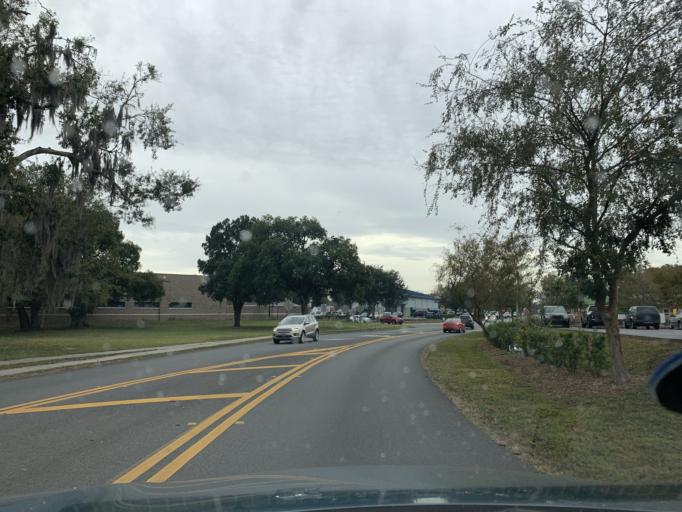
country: US
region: Florida
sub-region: Pasco County
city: Zephyrhills
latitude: 28.2452
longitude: -82.1872
